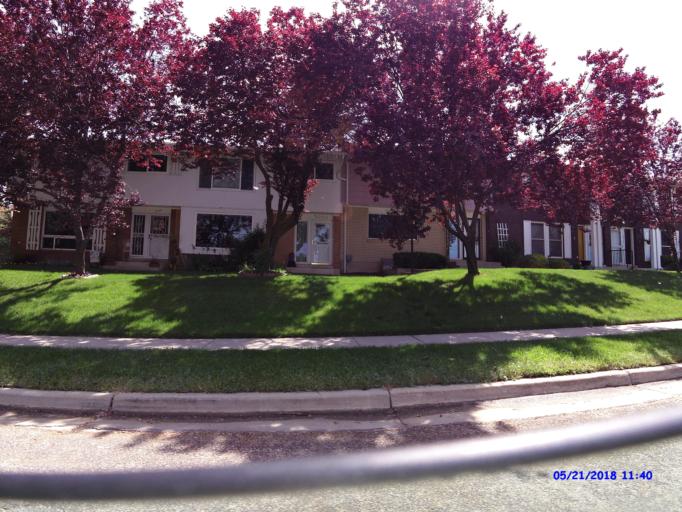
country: US
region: Utah
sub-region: Weber County
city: South Ogden
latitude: 41.1903
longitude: -111.9586
